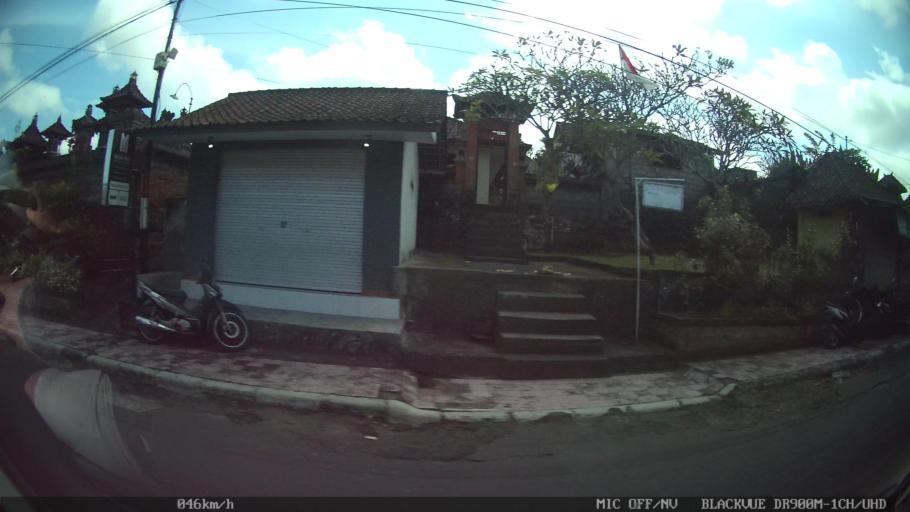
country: ID
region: Bali
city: Banjar Kelodan
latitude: -8.5327
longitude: 115.3287
